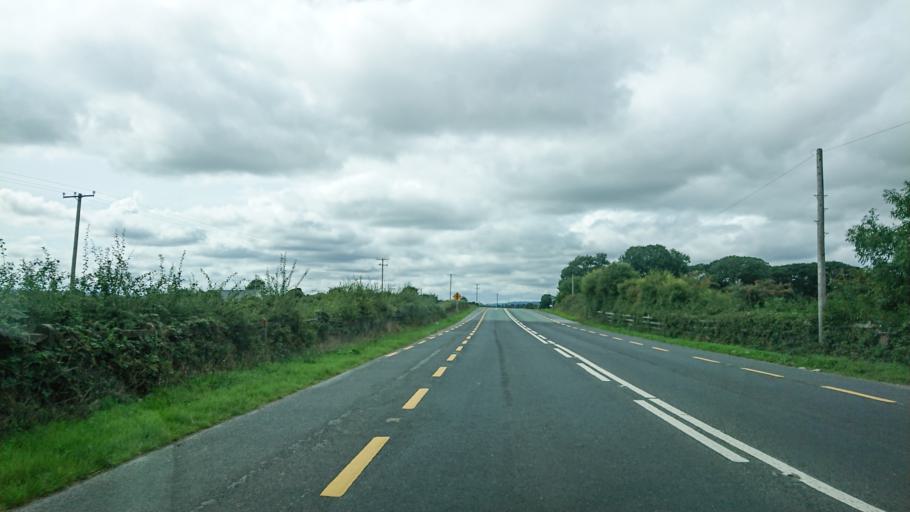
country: IE
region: Munster
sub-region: Waterford
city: Dungarvan
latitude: 52.1284
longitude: -7.7959
